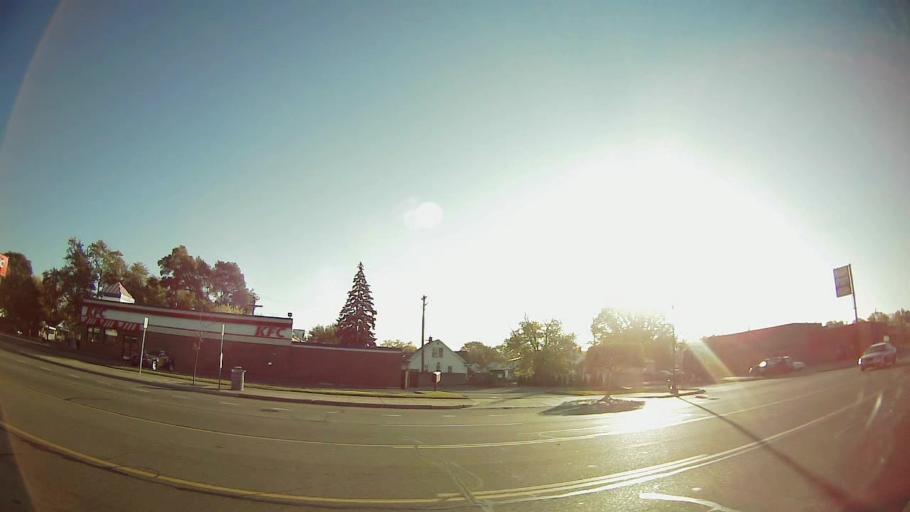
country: US
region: Michigan
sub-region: Macomb County
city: Warren
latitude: 42.4668
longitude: -83.0270
